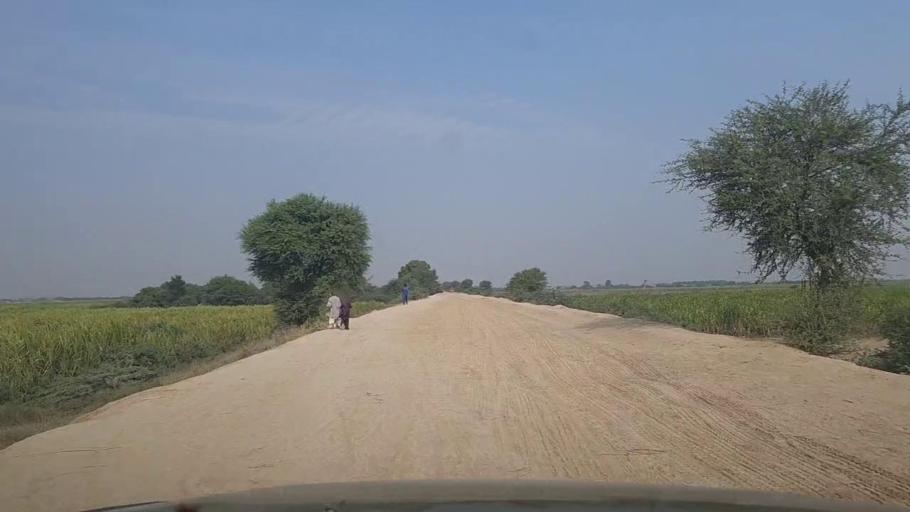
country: PK
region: Sindh
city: Bulri
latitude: 25.0254
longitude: 68.2816
